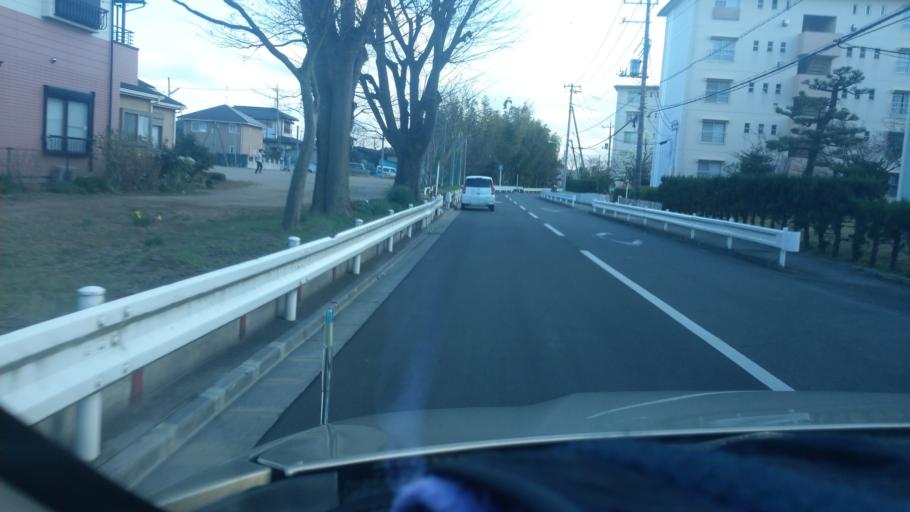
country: JP
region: Saitama
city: Yono
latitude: 35.8888
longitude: 139.5995
